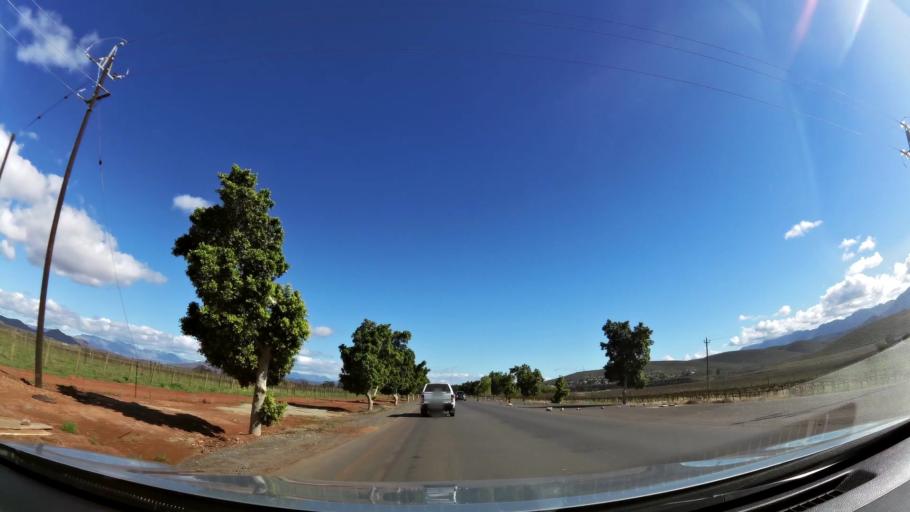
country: ZA
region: Western Cape
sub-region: Cape Winelands District Municipality
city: Ashton
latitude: -33.8309
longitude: 20.0795
